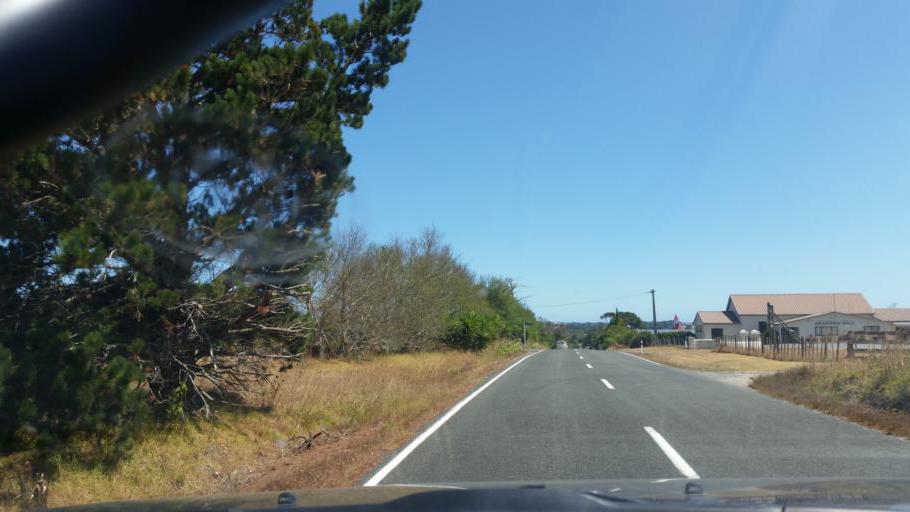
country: NZ
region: Northland
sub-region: Kaipara District
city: Dargaville
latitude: -36.0112
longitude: 173.9388
